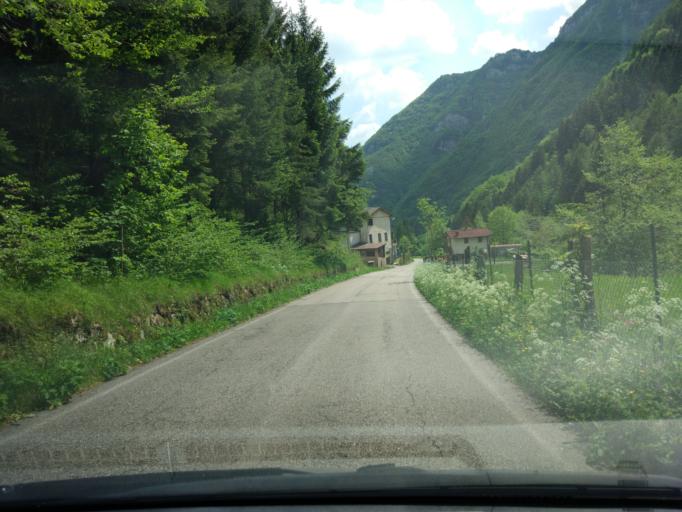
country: IT
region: Veneto
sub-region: Provincia di Verona
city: Selva di Progno
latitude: 45.6684
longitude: 11.1163
